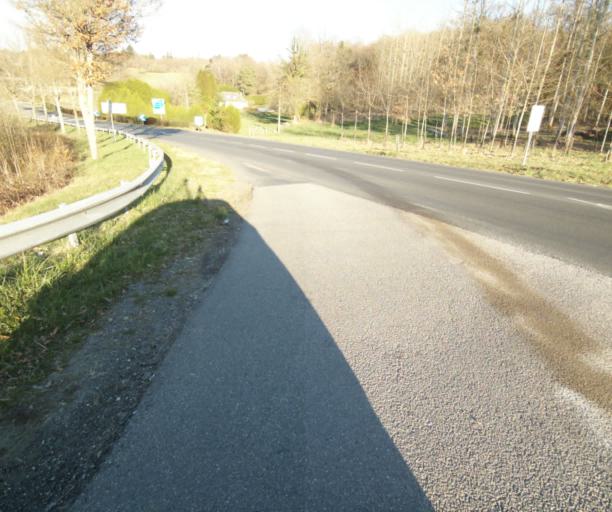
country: FR
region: Limousin
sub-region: Departement de la Correze
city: Seilhac
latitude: 45.3580
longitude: 1.7108
